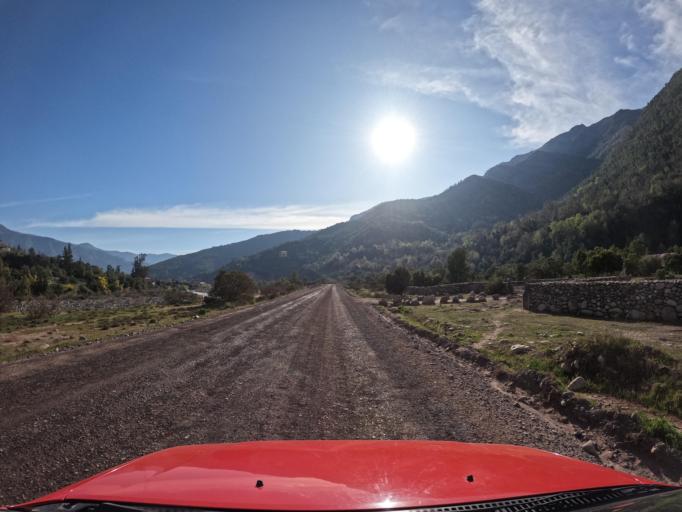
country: CL
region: O'Higgins
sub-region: Provincia de Colchagua
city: Chimbarongo
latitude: -34.9961
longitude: -70.8143
